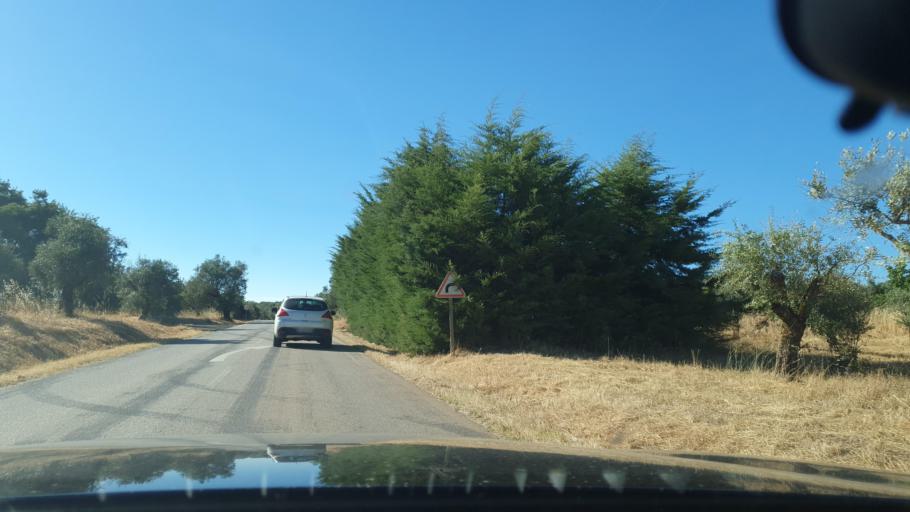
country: PT
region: Evora
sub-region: Vila Vicosa
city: Vila Vicosa
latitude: 38.7463
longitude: -7.4078
